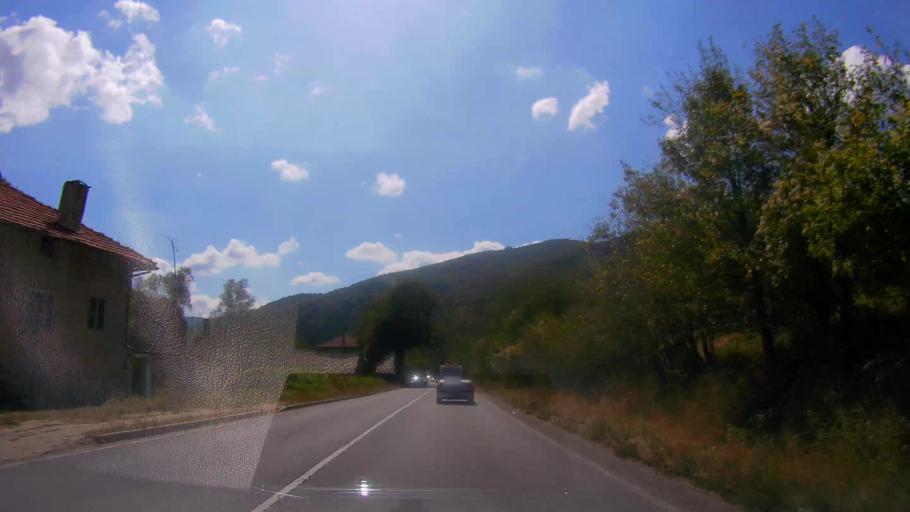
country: BG
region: Stara Zagora
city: Gurkovo
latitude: 42.7412
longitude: 25.7080
